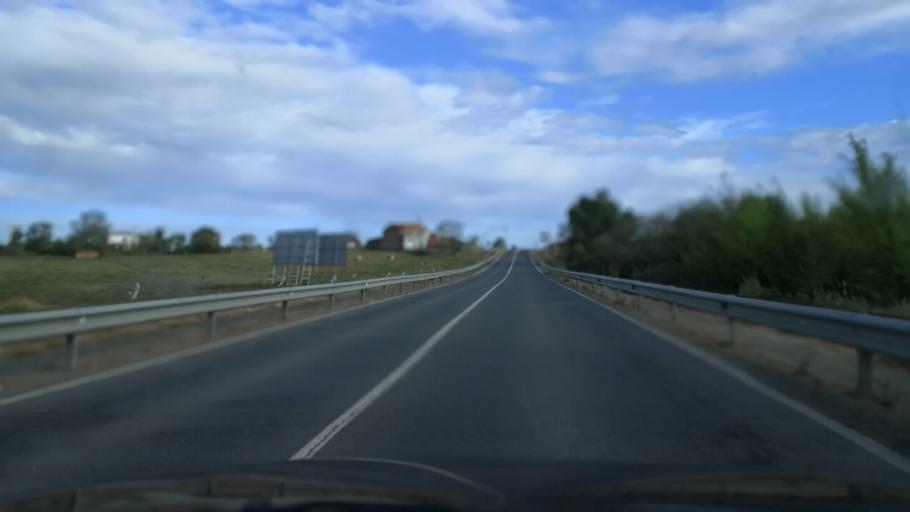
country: ES
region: Extremadura
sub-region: Provincia de Caceres
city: Moraleja
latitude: 40.0626
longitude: -6.6505
